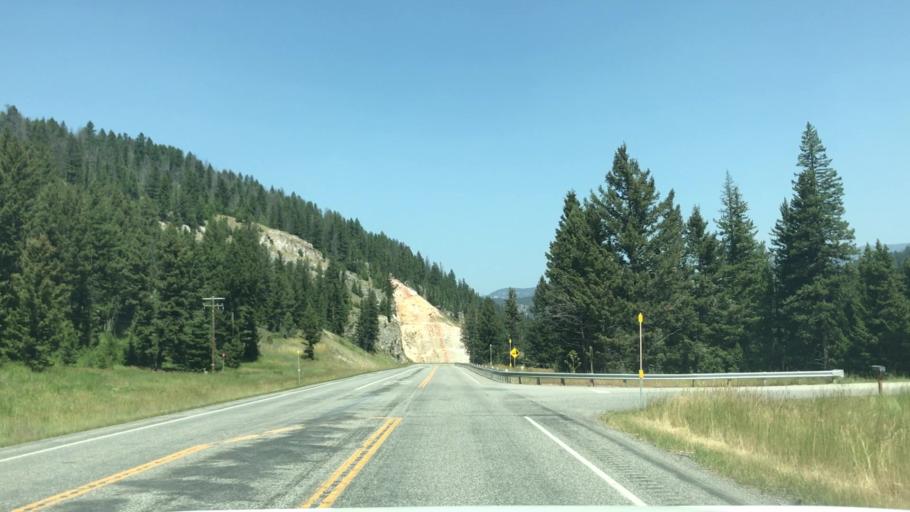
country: US
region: Montana
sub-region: Gallatin County
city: Big Sky
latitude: 45.1737
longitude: -111.2432
